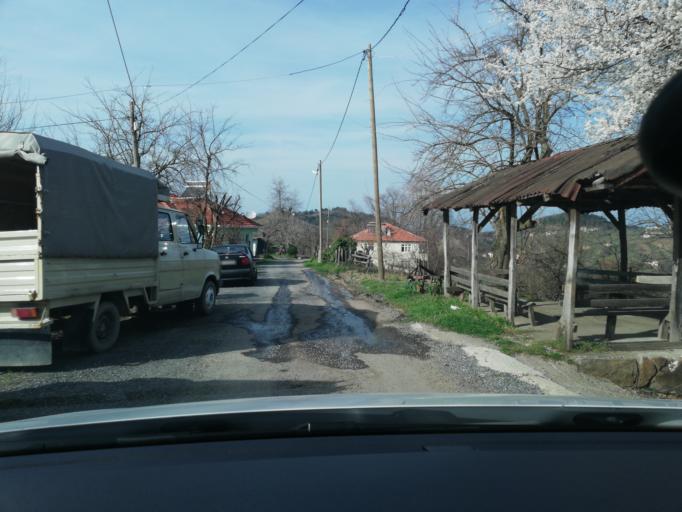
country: TR
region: Zonguldak
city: Kozlu
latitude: 41.3558
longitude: 31.6286
